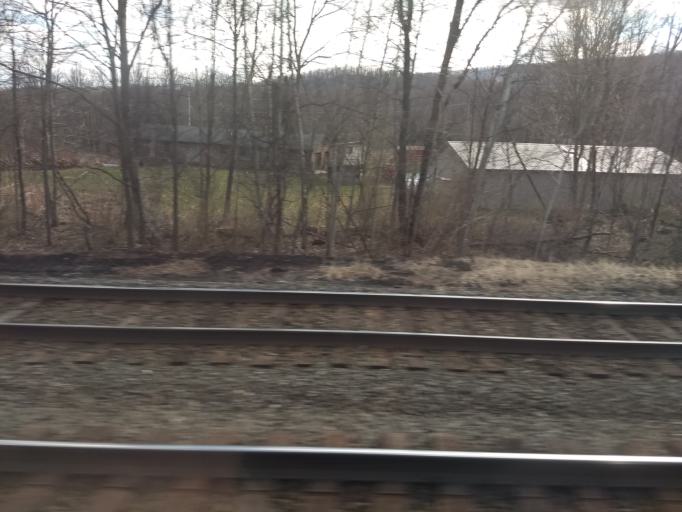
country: US
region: Pennsylvania
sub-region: Blair County
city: Bellwood
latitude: 40.6198
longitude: -78.3221
